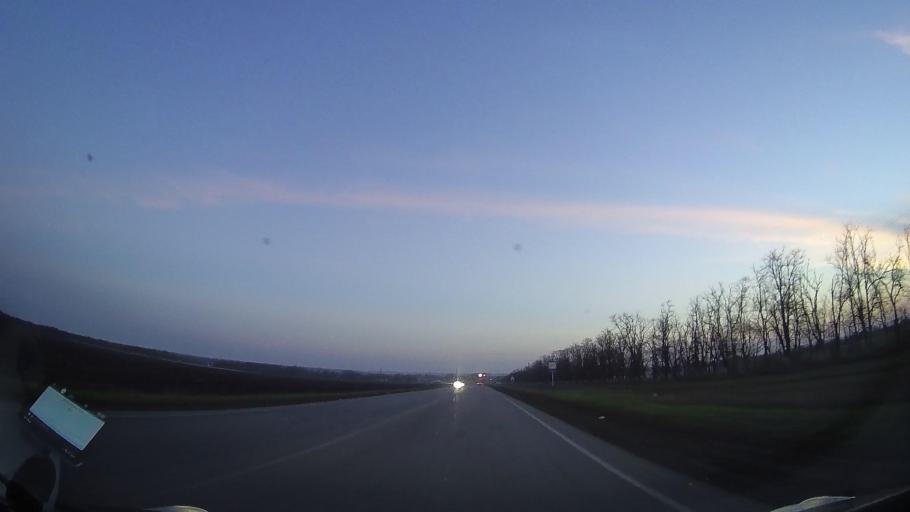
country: RU
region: Rostov
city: Zernograd
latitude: 46.8171
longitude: 40.2994
